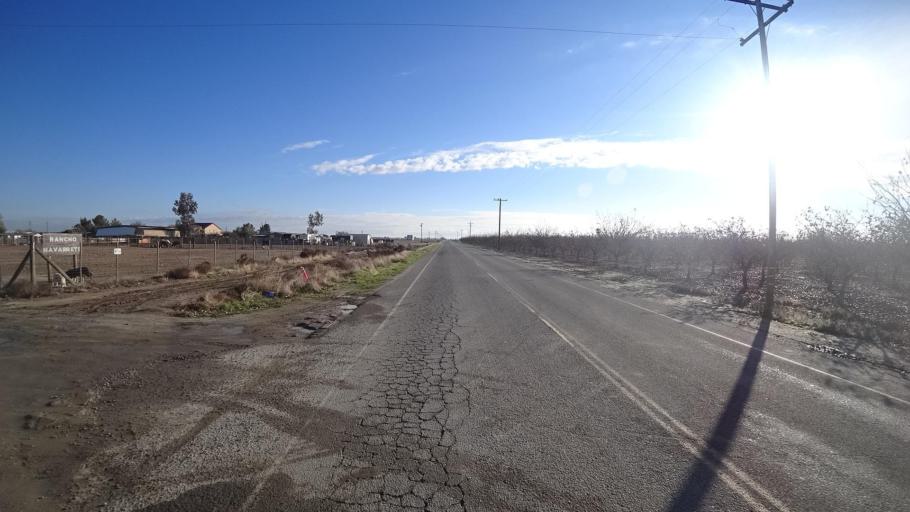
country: US
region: California
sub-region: Kern County
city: Delano
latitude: 35.7761
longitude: -119.3345
